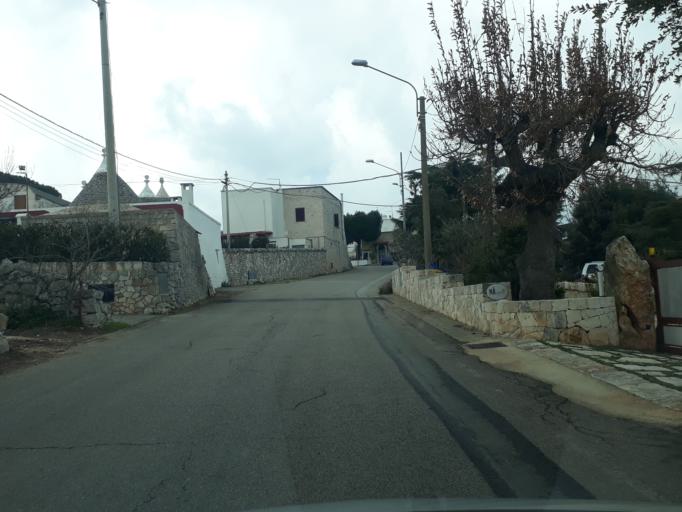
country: IT
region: Apulia
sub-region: Provincia di Brindisi
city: Lamie di Olimpie-Selva
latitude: 40.7909
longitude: 17.3198
